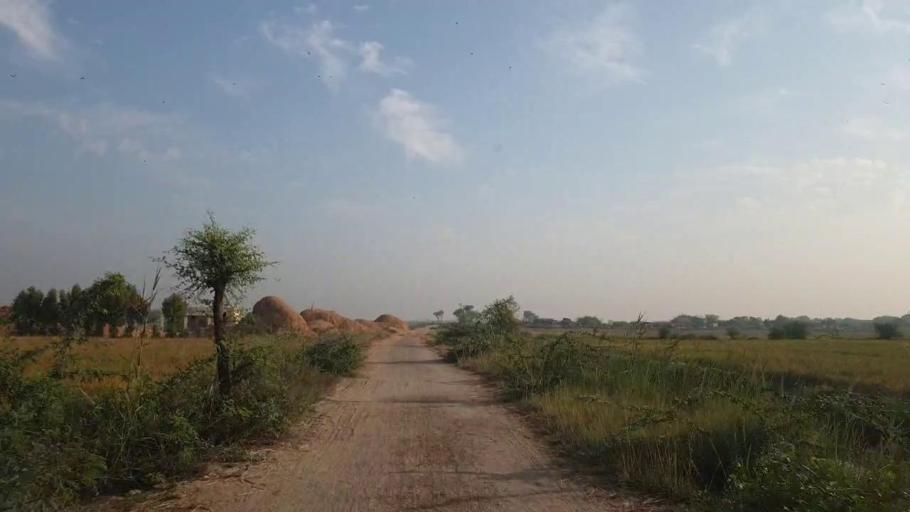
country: PK
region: Sindh
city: Tando Bago
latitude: 24.8188
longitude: 68.9565
